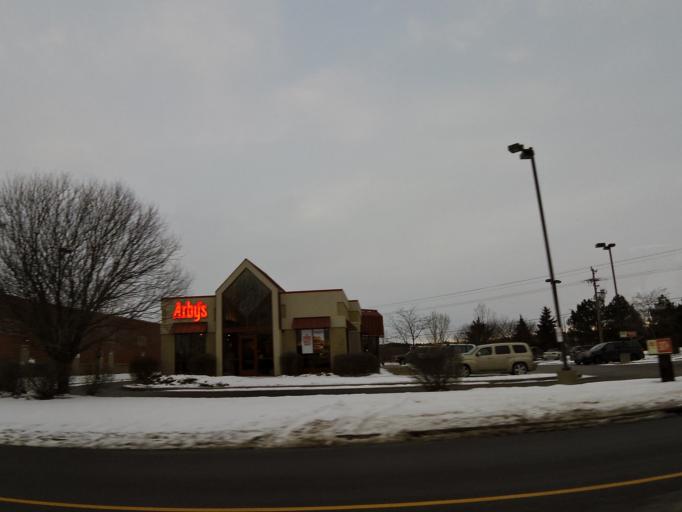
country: US
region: Minnesota
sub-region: Washington County
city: Stillwater
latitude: 45.0346
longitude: -92.8454
